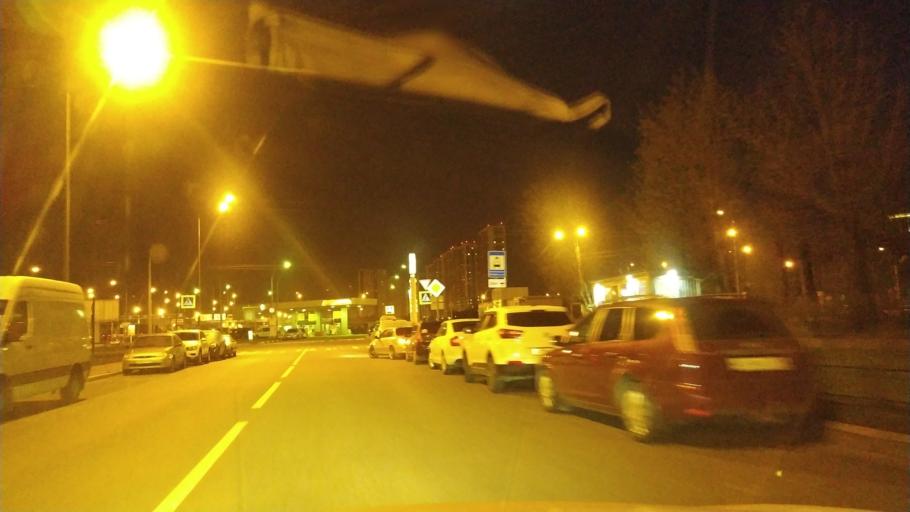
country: RU
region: St.-Petersburg
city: Kupchino
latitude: 59.8364
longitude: 30.3705
